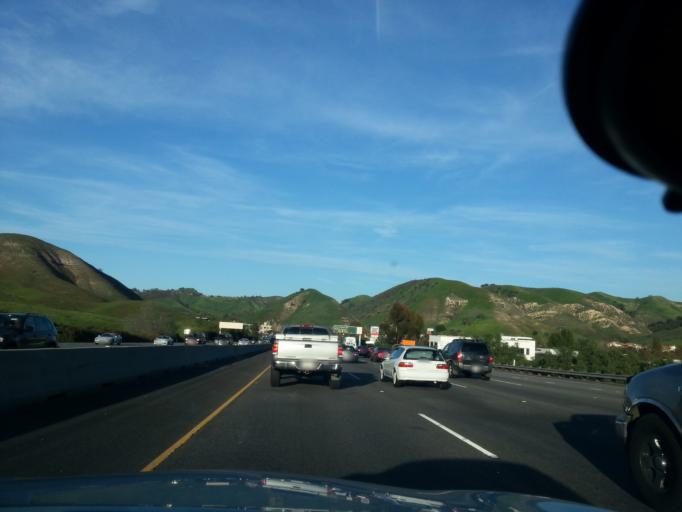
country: US
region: California
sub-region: Los Angeles County
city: Agoura
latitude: 34.1423
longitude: -118.7063
